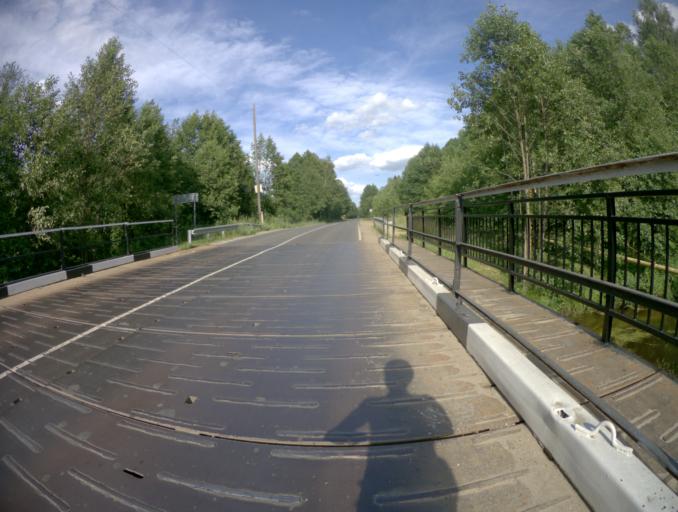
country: RU
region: Vladimir
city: Galitsy
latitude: 56.2868
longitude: 42.7948
